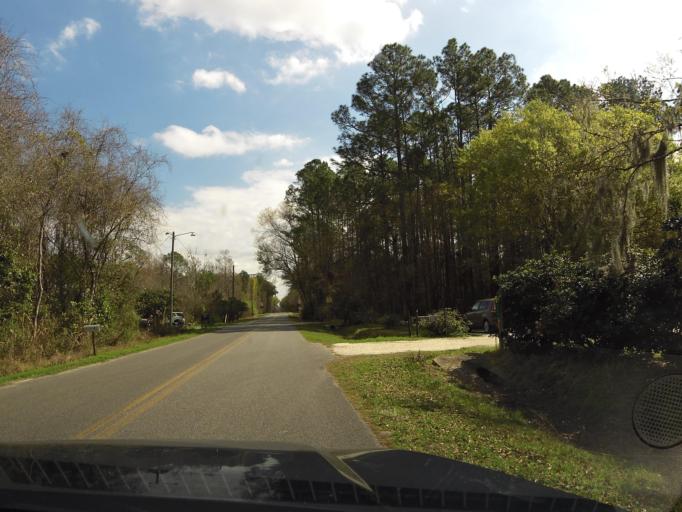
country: US
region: Florida
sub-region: Bradford County
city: Starke
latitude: 29.9864
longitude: -82.0947
